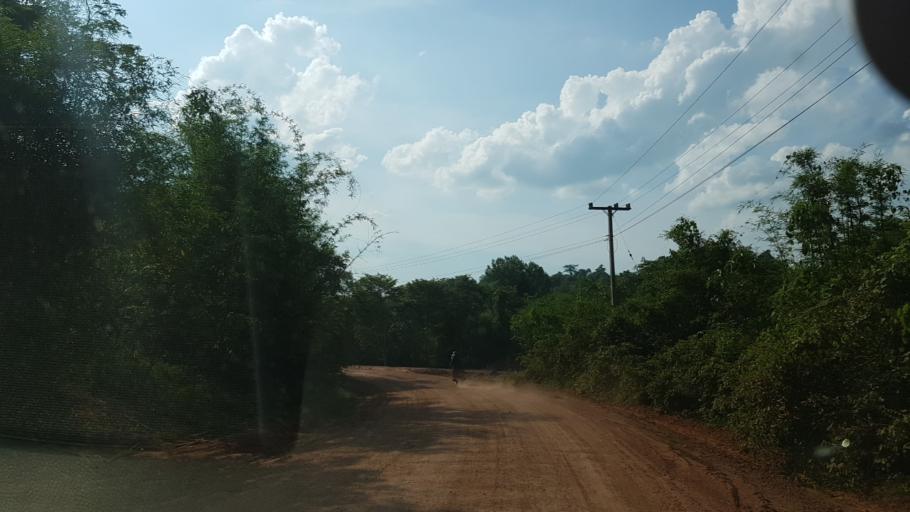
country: LA
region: Vientiane
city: Muang Phon-Hong
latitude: 18.3511
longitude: 102.2809
